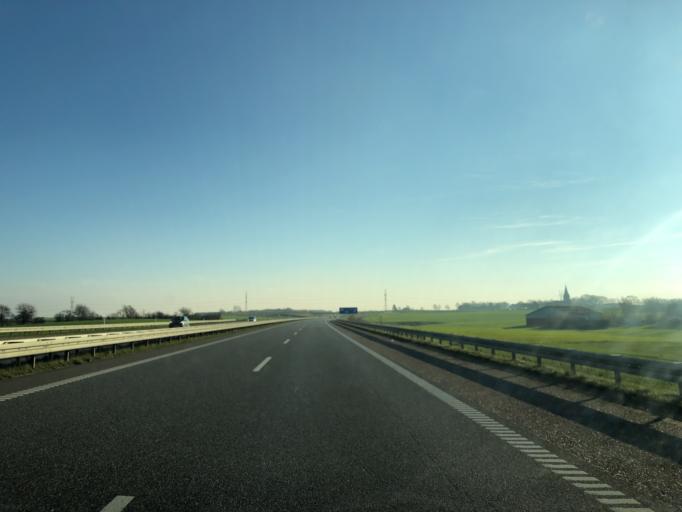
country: DK
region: Central Jutland
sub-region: Hedensted Kommune
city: Torring
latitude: 55.8097
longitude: 9.5574
